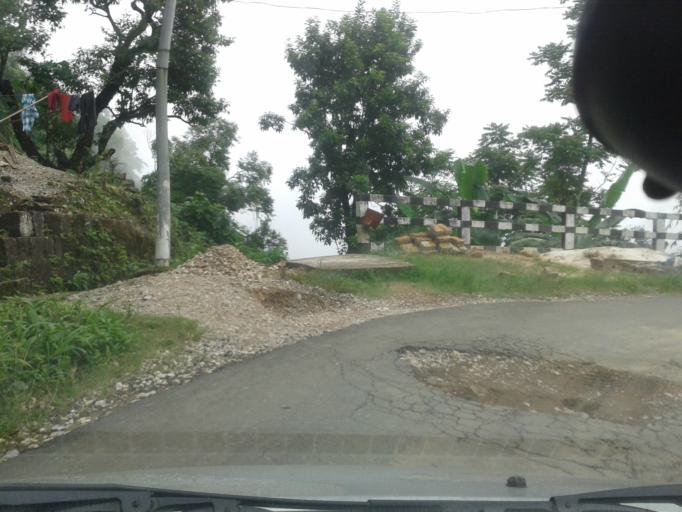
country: IN
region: Meghalaya
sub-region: East Khasi Hills
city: Cherrapunji
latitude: 25.2099
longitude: 91.7434
